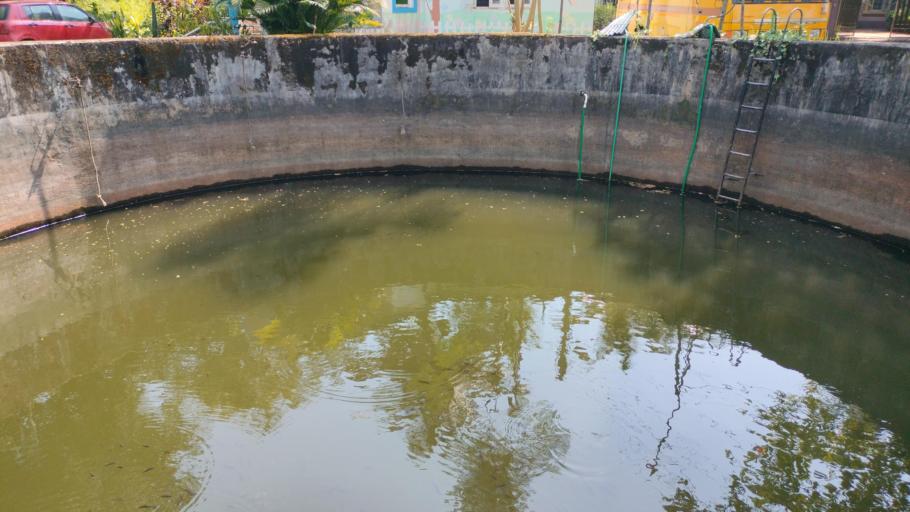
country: IN
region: Maharashtra
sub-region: Thane
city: Bhayandar
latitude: 19.3431
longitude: 72.8174
